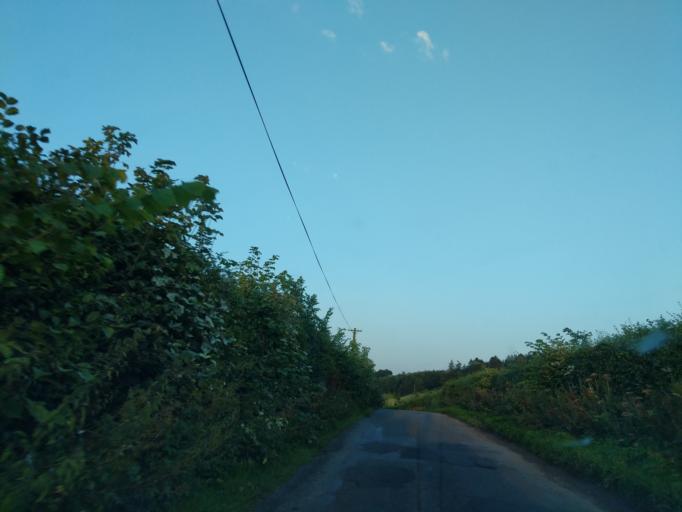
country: GB
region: Scotland
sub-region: Stirling
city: Doune
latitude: 56.1231
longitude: -4.0749
